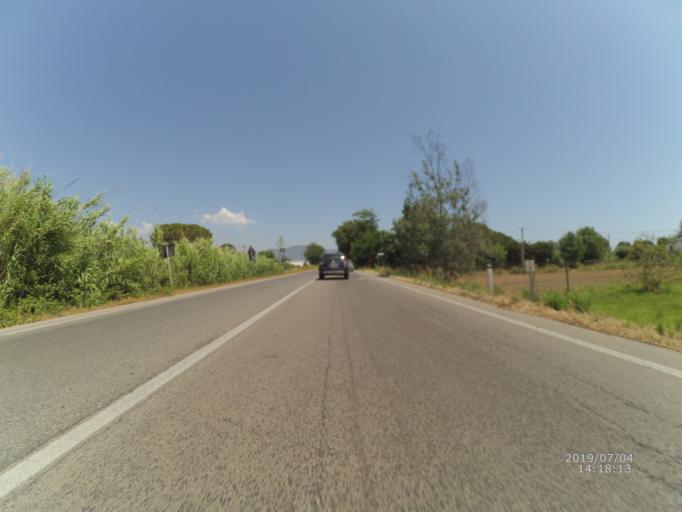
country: IT
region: Latium
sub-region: Provincia di Latina
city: Sperlonga
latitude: 41.2887
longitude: 13.3720
